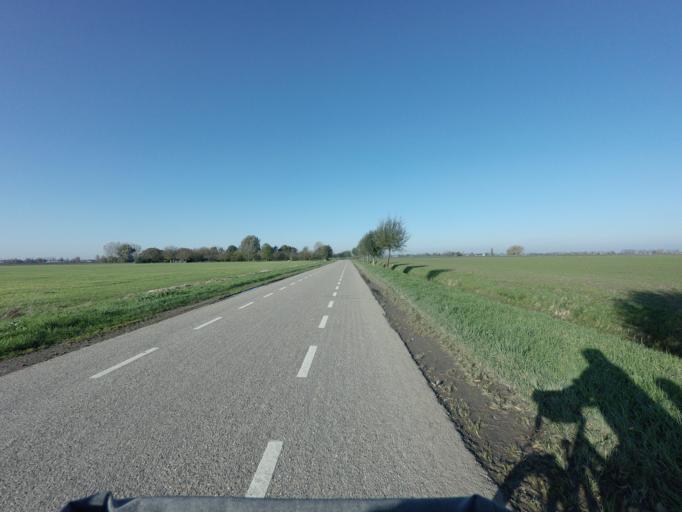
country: NL
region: North Brabant
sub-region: Gemeente Waalwijk
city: Waalwijk
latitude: 51.7418
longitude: 5.0636
